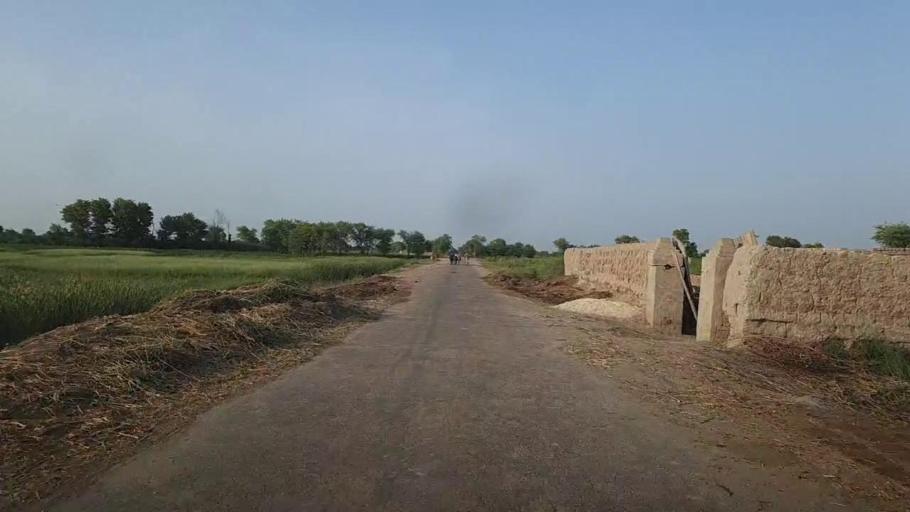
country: PK
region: Sindh
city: Ubauro
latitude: 28.1220
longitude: 69.8269
